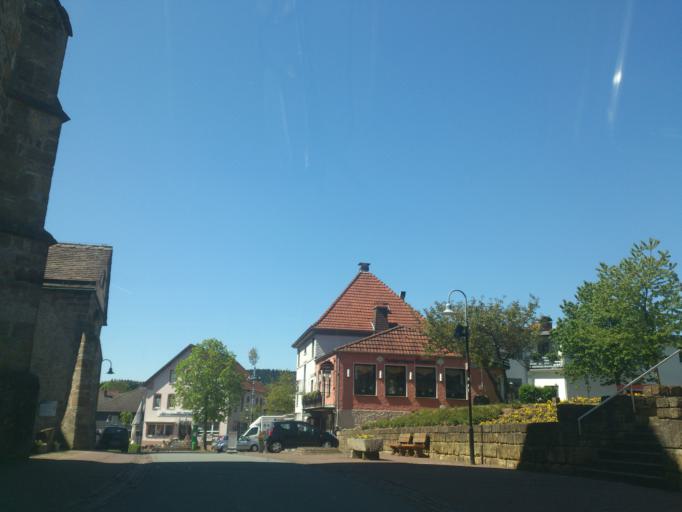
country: DE
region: North Rhine-Westphalia
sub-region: Regierungsbezirk Detmold
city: Bad Driburg
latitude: 51.6763
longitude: 8.9996
